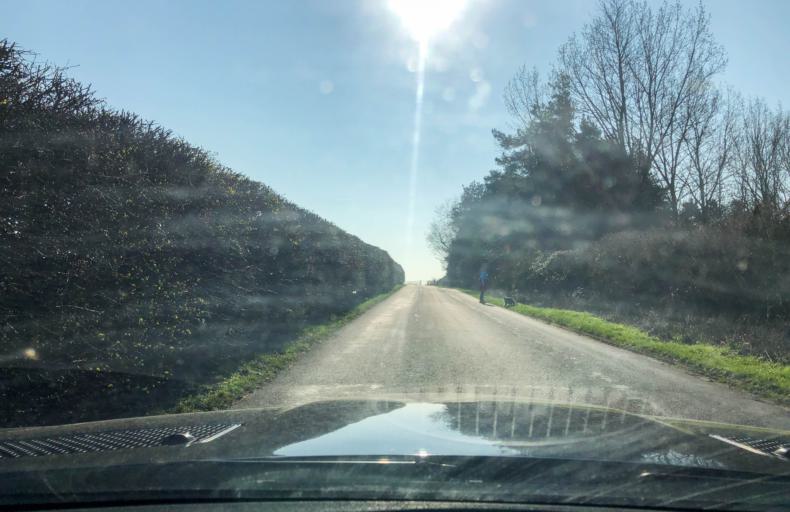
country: GB
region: England
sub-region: Warwickshire
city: Wellesbourne Mountford
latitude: 52.1868
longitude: -1.5399
